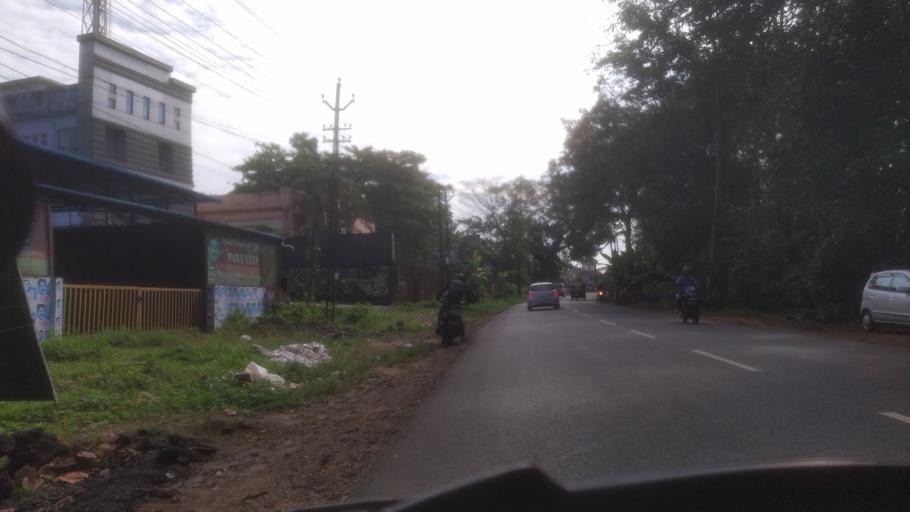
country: IN
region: Kerala
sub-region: Ernakulam
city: Kotamangalam
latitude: 10.0586
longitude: 76.6798
